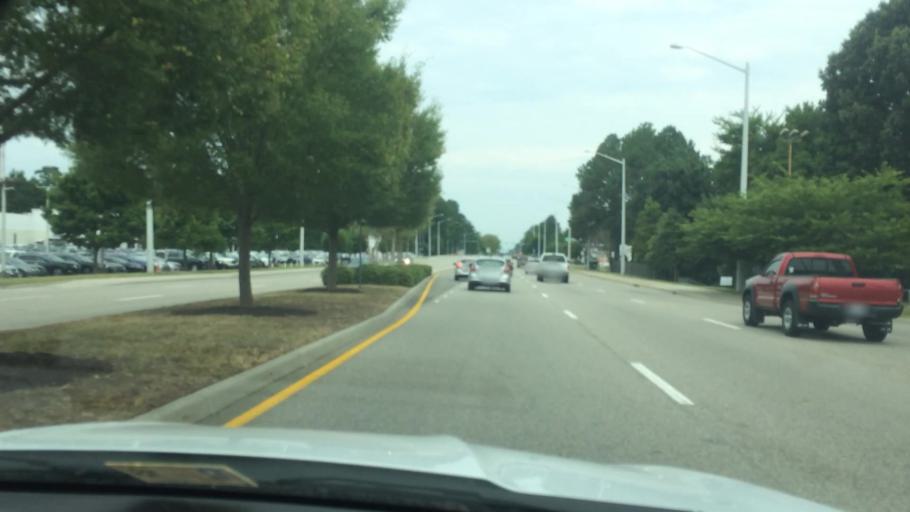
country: US
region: Virginia
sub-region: York County
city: Yorktown
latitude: 37.1522
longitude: -76.5307
